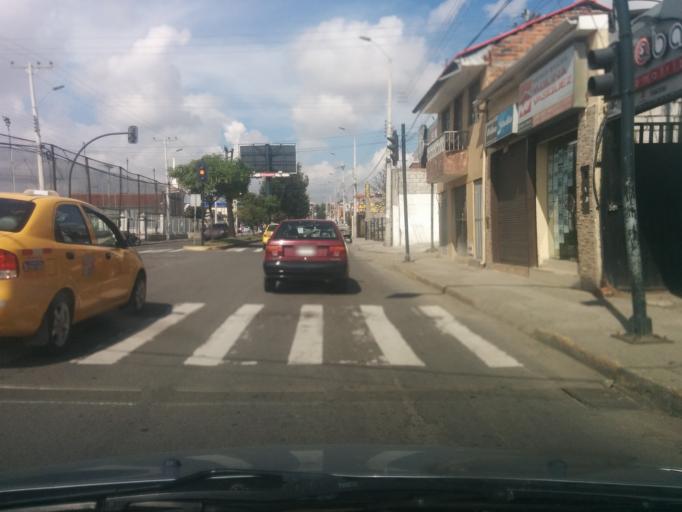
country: EC
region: Azuay
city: Cuenca
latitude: -2.8981
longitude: -78.9816
